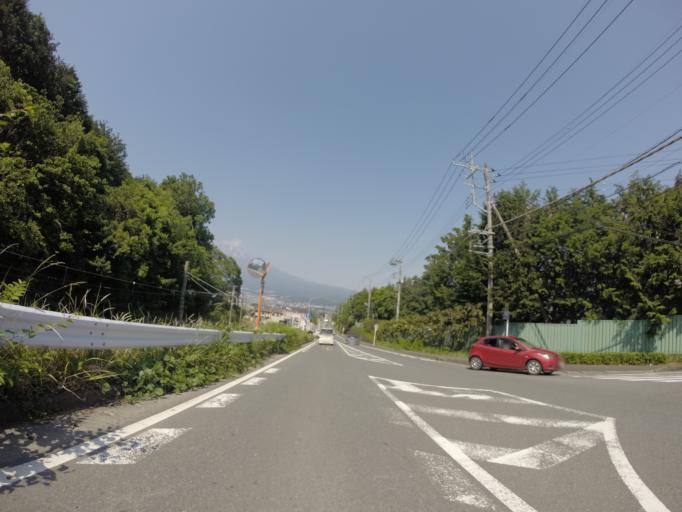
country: JP
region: Shizuoka
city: Fujinomiya
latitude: 35.2174
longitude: 138.5922
